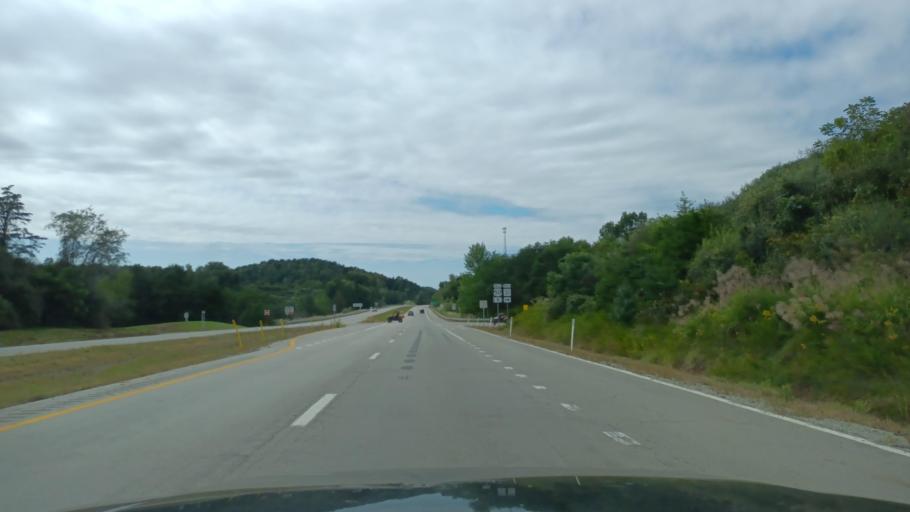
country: US
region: Ohio
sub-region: Washington County
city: Reno
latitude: 39.2514
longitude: -81.3257
